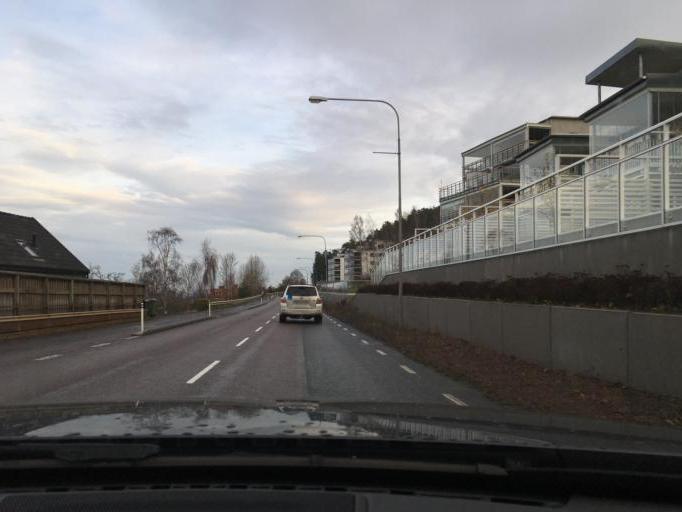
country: SE
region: Joenkoeping
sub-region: Jonkopings Kommun
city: Graenna
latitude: 58.0096
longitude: 14.4557
